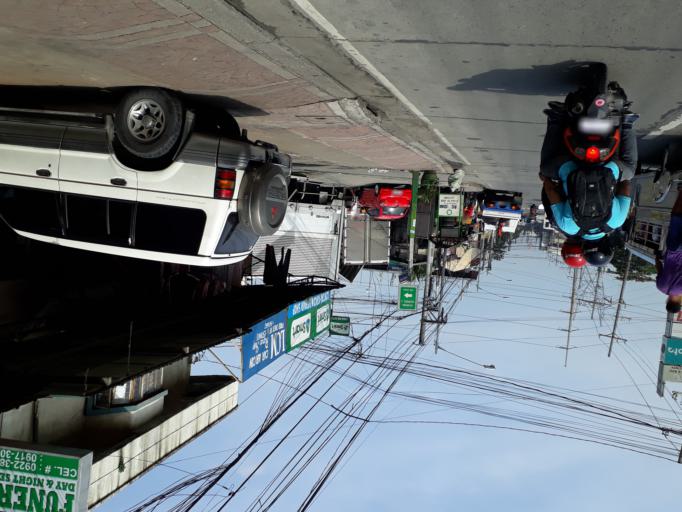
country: PH
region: Calabarzon
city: Bagong Pagasa
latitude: 14.6735
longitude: 121.0133
